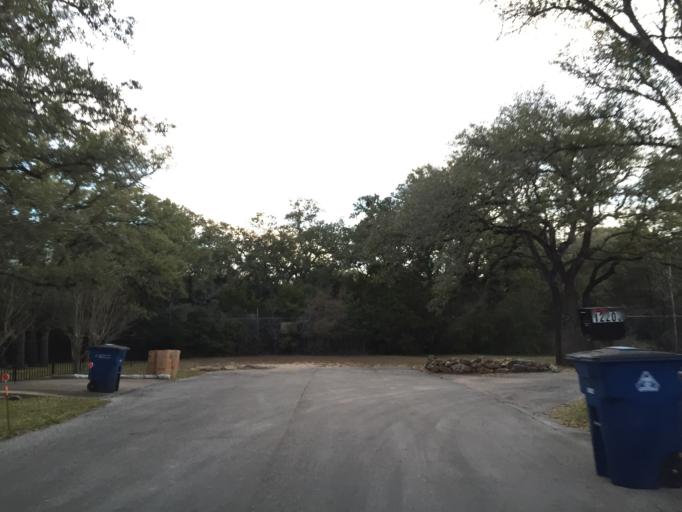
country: US
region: Texas
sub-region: Williamson County
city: Jollyville
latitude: 30.4264
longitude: -97.7470
